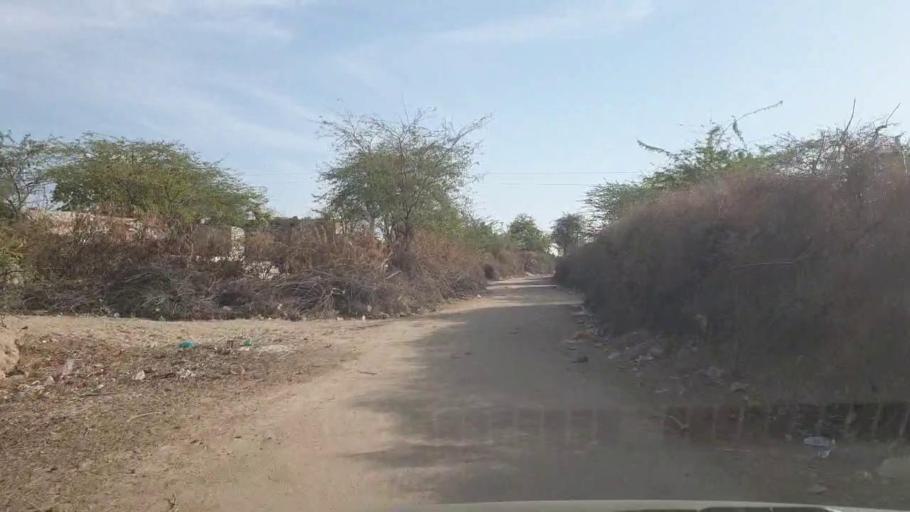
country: PK
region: Sindh
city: Nabisar
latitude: 25.0624
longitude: 69.6425
